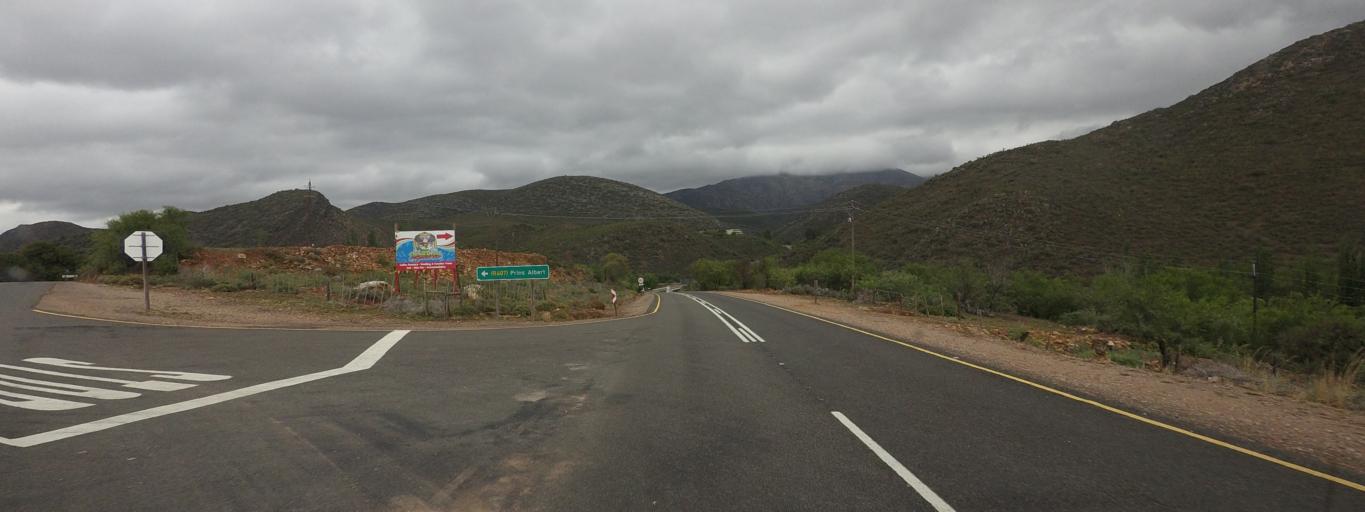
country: ZA
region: Western Cape
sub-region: Eden District Municipality
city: Oudtshoorn
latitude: -33.4017
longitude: 22.2164
